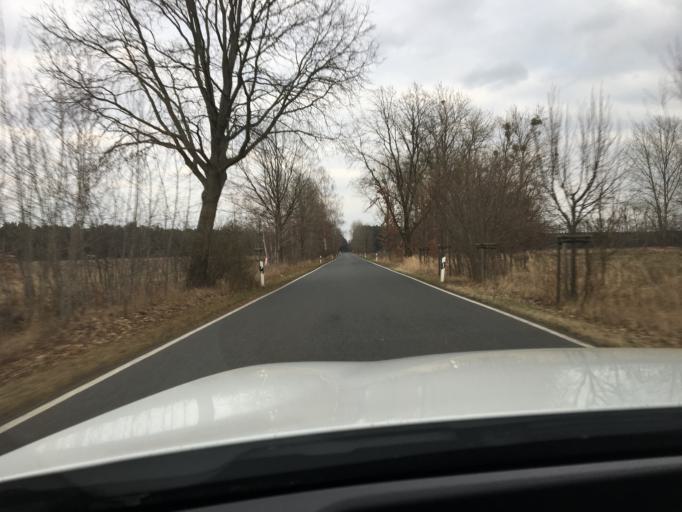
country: DE
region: Brandenburg
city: Liebenwalde
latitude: 52.8842
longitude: 13.4642
